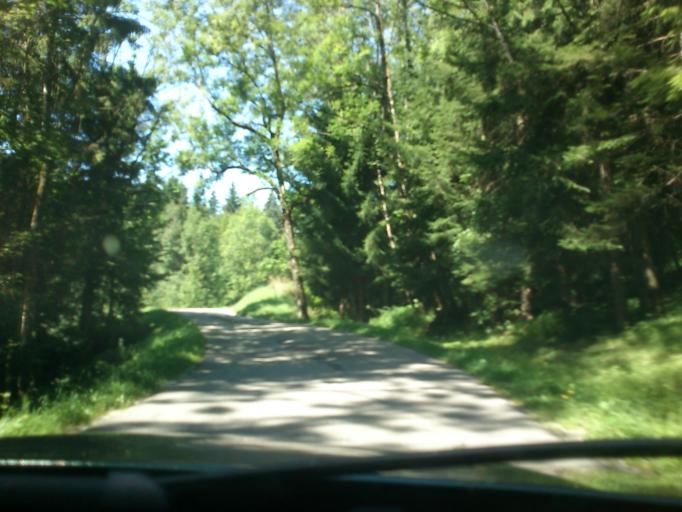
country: AT
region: Upper Austria
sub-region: Politischer Bezirk Kirchdorf an der Krems
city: Rossleithen
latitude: 47.7242
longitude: 14.3566
